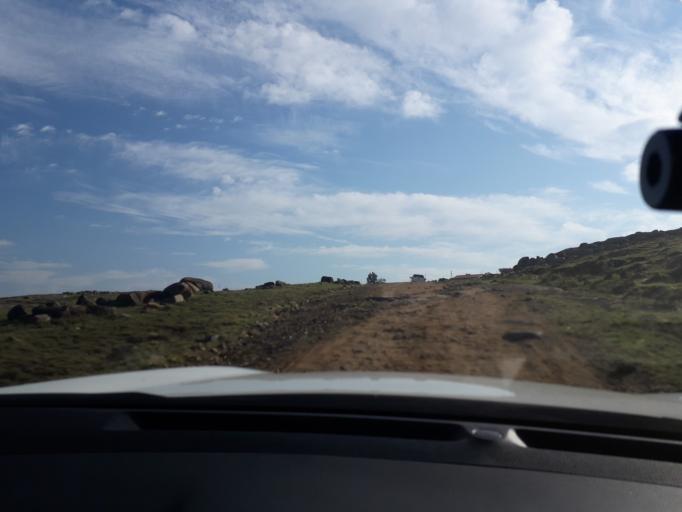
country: ZA
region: Eastern Cape
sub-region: Buffalo City Metropolitan Municipality
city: Bhisho
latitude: -32.9427
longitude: 27.2893
